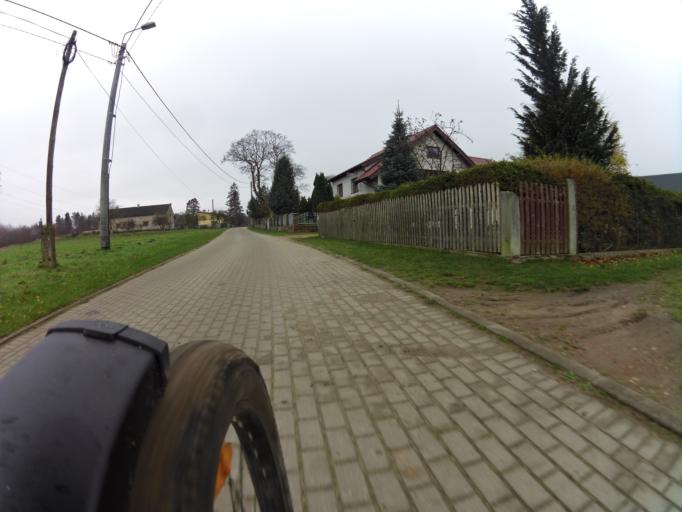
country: PL
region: Pomeranian Voivodeship
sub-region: Powiat pucki
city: Krokowa
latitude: 54.7228
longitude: 18.1361
